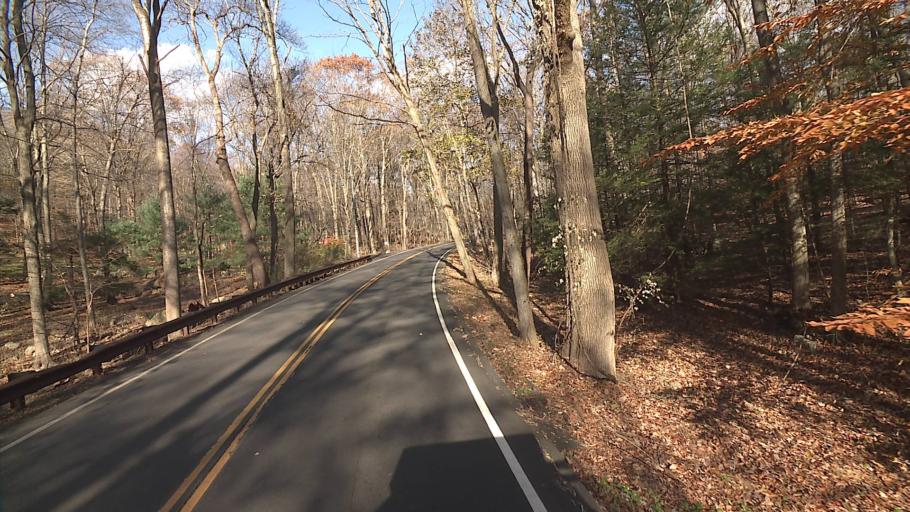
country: US
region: Connecticut
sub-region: Fairfield County
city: Georgetown
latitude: 41.2733
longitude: -73.3810
